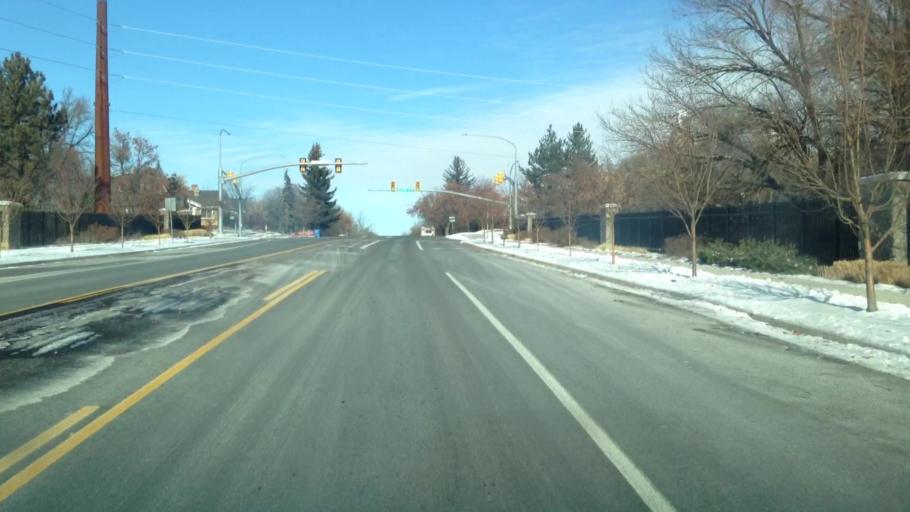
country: US
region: Utah
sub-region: Cache County
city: Logan
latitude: 41.7304
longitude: -111.8298
